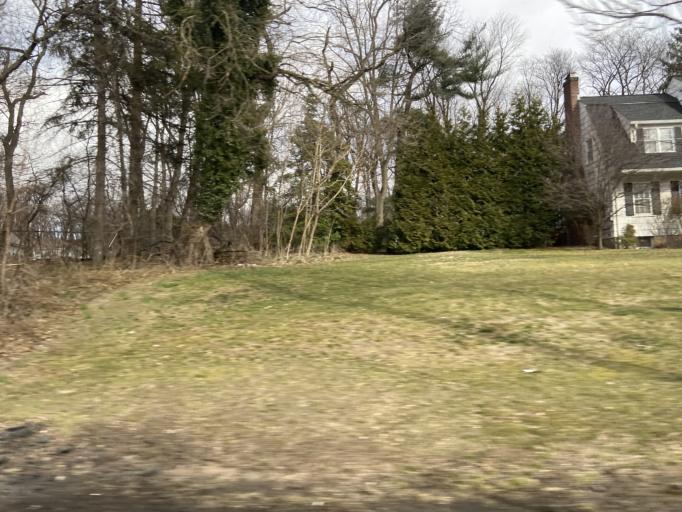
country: US
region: New Jersey
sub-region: Bergen County
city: Paramus
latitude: 40.9284
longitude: -74.0907
